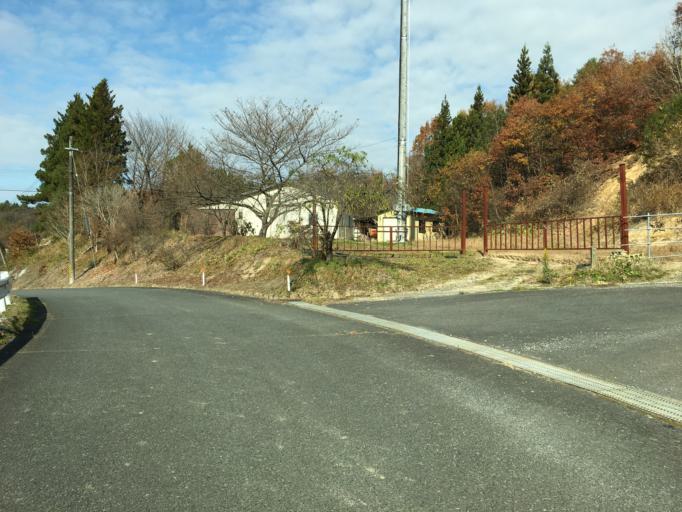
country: JP
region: Fukushima
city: Ishikawa
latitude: 37.1739
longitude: 140.5529
